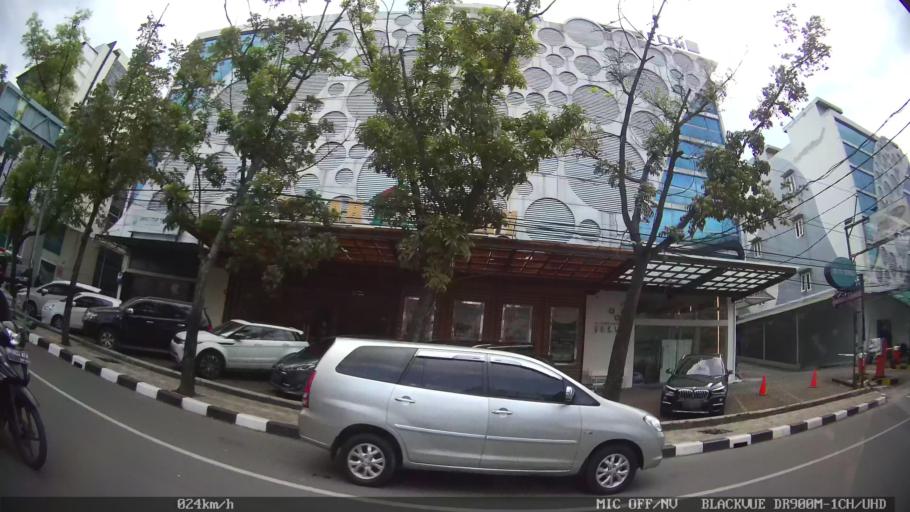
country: ID
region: North Sumatra
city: Medan
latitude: 3.5793
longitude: 98.6837
